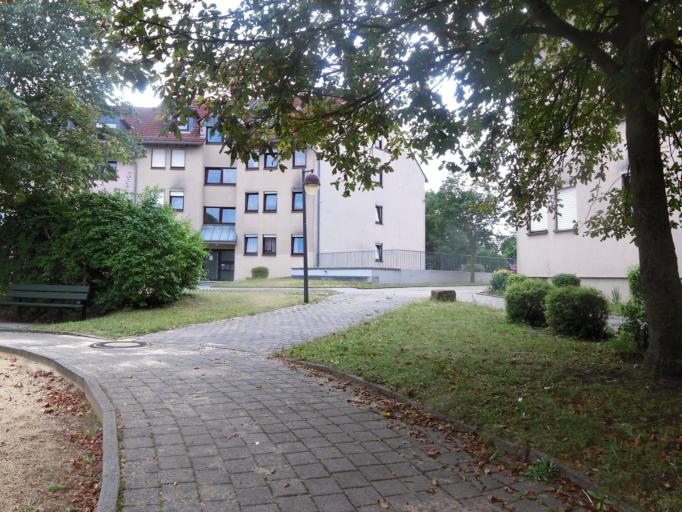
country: DE
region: Bavaria
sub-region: Regierungsbezirk Unterfranken
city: Randersacker
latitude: 49.7385
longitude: 9.9632
